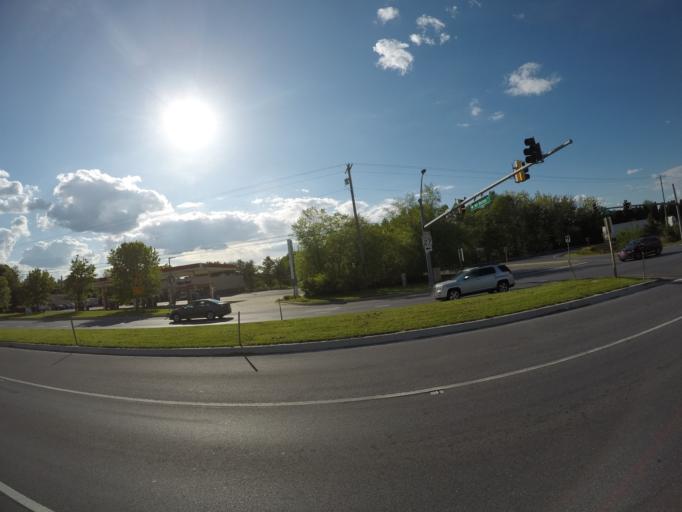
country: US
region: Maryland
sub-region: Carroll County
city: Mount Airy
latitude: 39.3529
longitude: -77.1683
